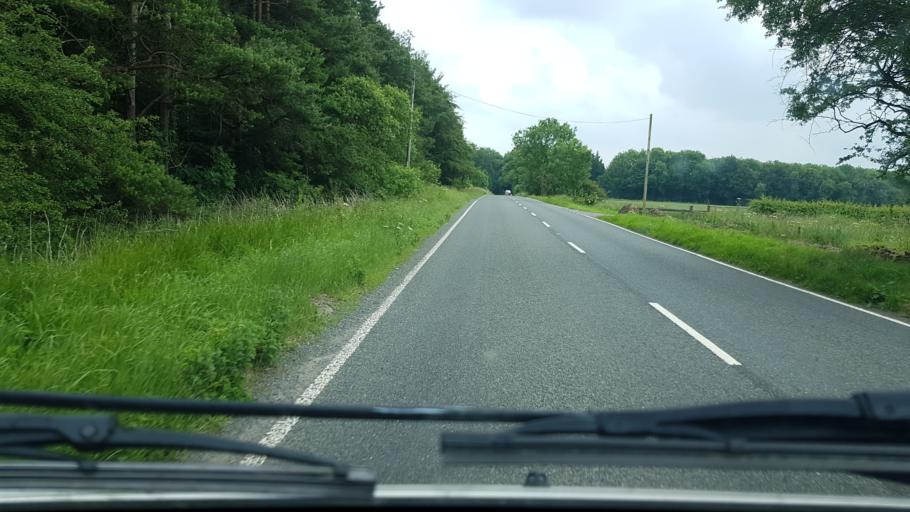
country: GB
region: England
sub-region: Gloucestershire
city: Donnington
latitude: 51.9861
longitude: -1.7709
